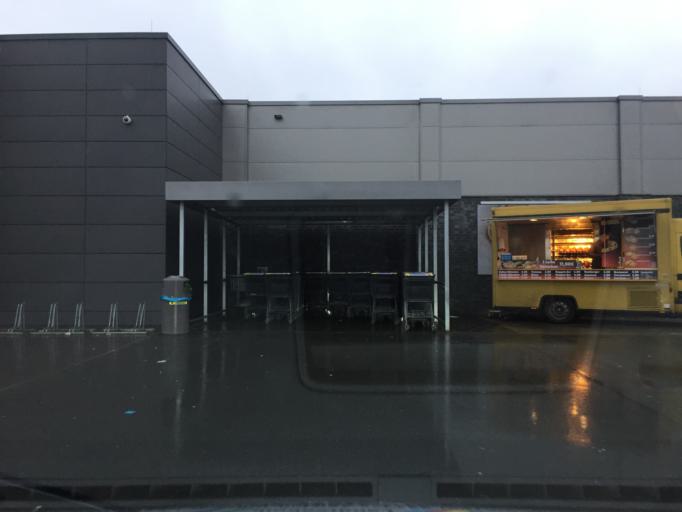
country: DE
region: Lower Saxony
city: Thedinghausen
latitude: 52.9609
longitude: 9.0188
